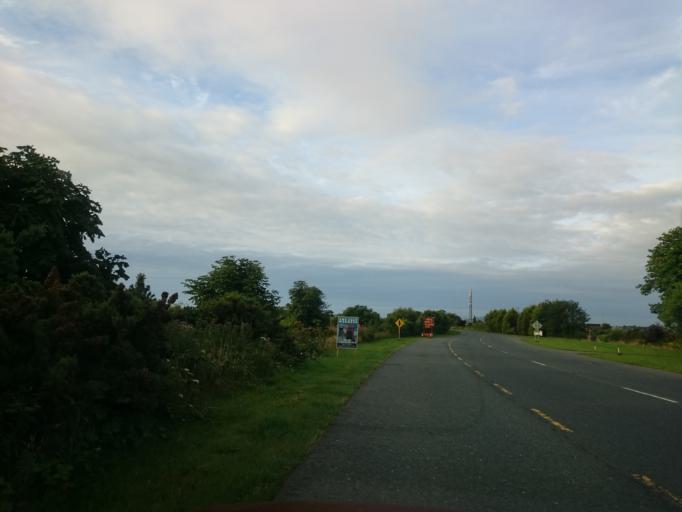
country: IE
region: Leinster
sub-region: Wicklow
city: Arklow
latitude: 52.8195
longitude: -6.1444
